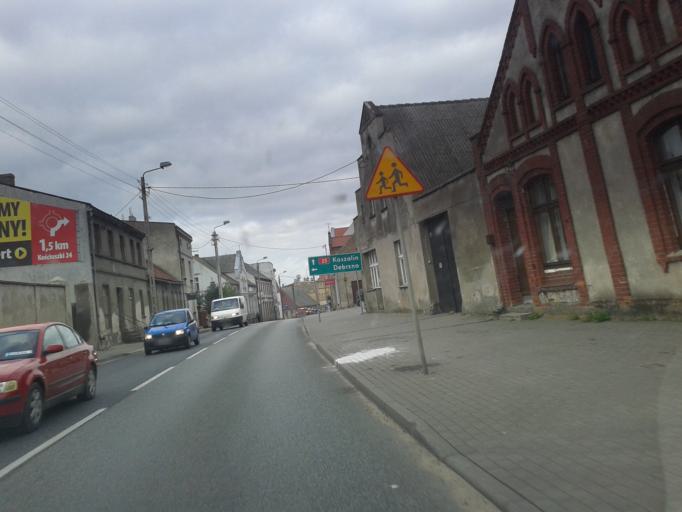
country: PL
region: Kujawsko-Pomorskie
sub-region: Powiat sepolenski
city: Sepolno Krajenskie
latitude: 53.4492
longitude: 17.5288
